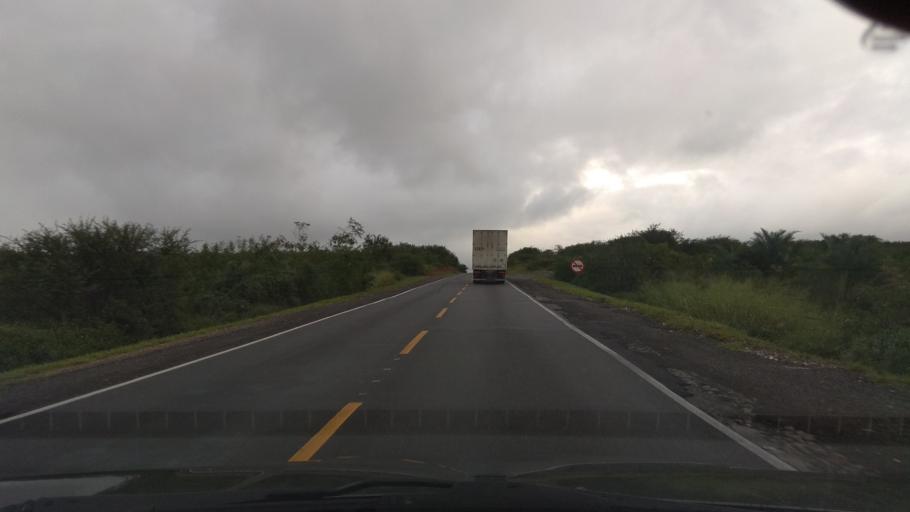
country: BR
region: Bahia
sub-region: Jaguaquara
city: Jaguaquara
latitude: -13.3788
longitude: -40.0204
